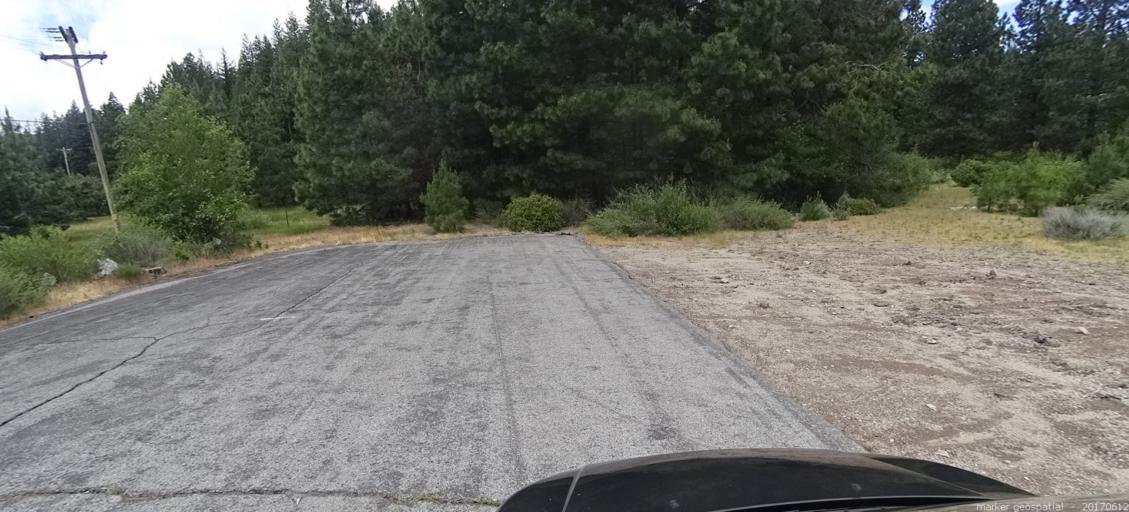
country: US
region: California
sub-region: Siskiyou County
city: Weed
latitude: 41.3680
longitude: -122.3727
